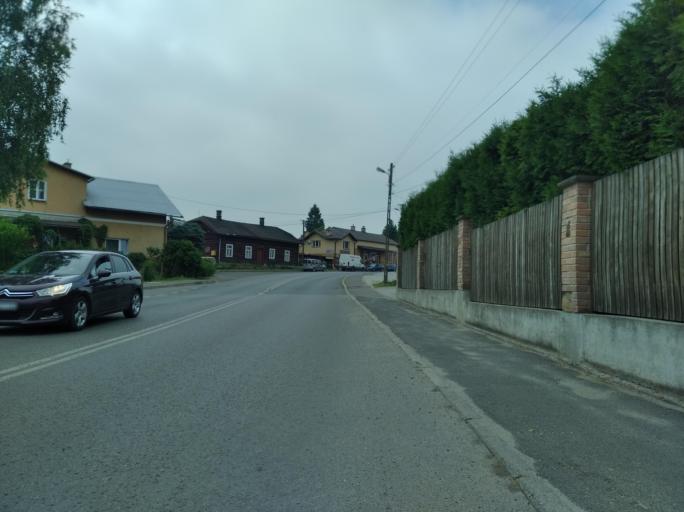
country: PL
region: Subcarpathian Voivodeship
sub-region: Powiat brzozowski
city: Haczow
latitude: 49.6686
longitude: 21.8915
